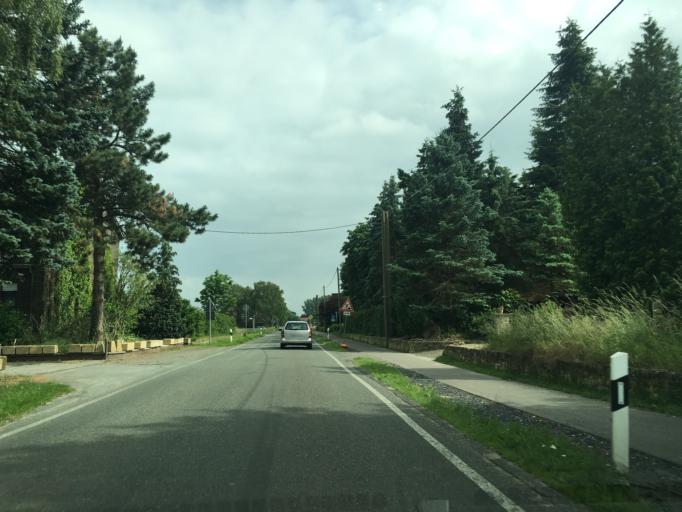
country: DE
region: North Rhine-Westphalia
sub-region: Regierungsbezirk Munster
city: Horstmar
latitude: 52.1106
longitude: 7.2991
